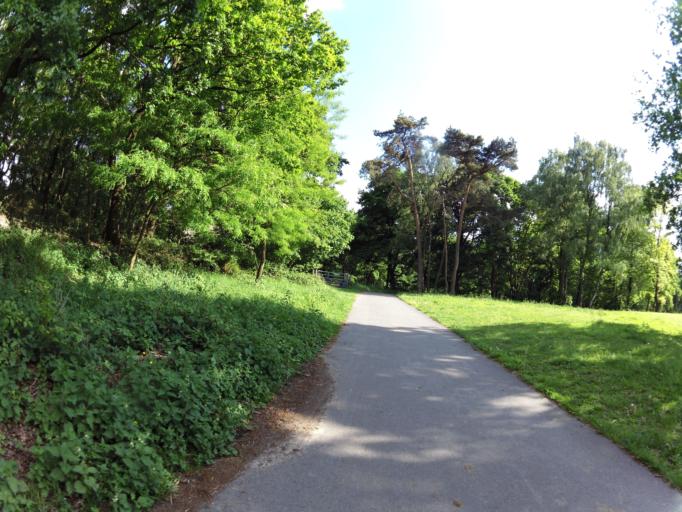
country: NL
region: Limburg
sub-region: Gemeente Brunssum
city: Brunssum
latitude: 50.9222
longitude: 5.9803
